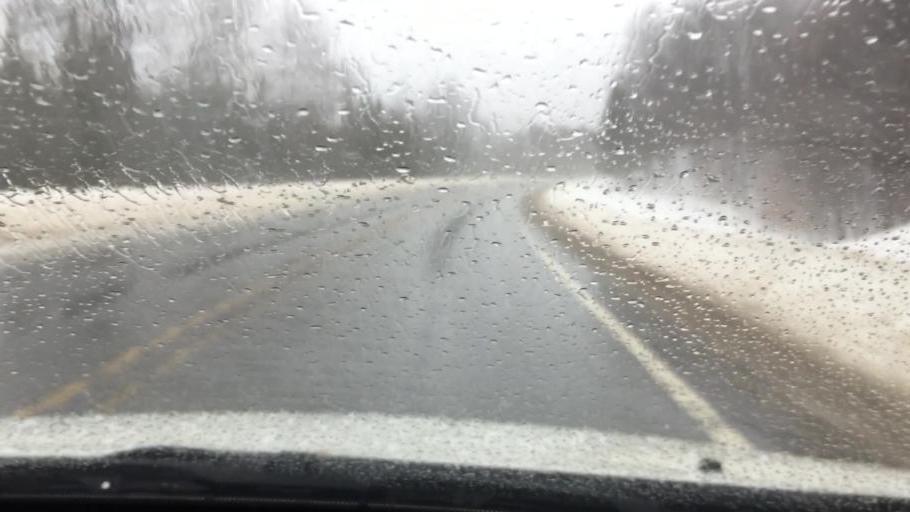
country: US
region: Michigan
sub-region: Antrim County
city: Mancelona
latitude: 44.9975
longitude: -85.0617
